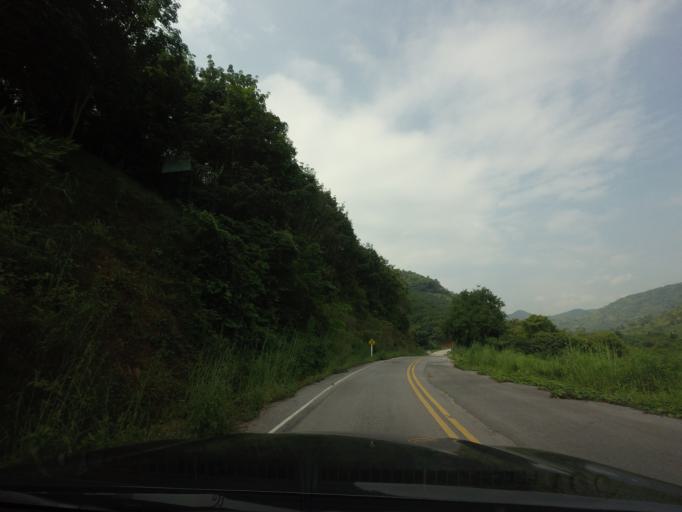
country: LA
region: Xiagnabouli
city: Muang Kenthao
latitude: 17.7745
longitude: 101.5385
